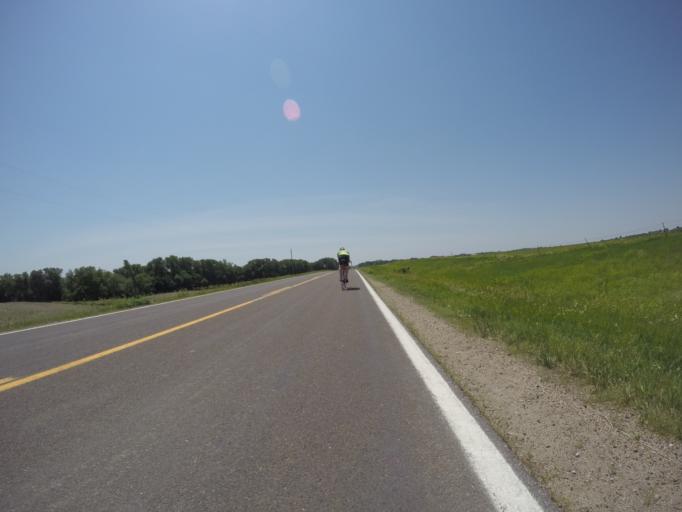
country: US
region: Nebraska
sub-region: Pawnee County
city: Pawnee City
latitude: 40.0115
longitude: -96.0484
